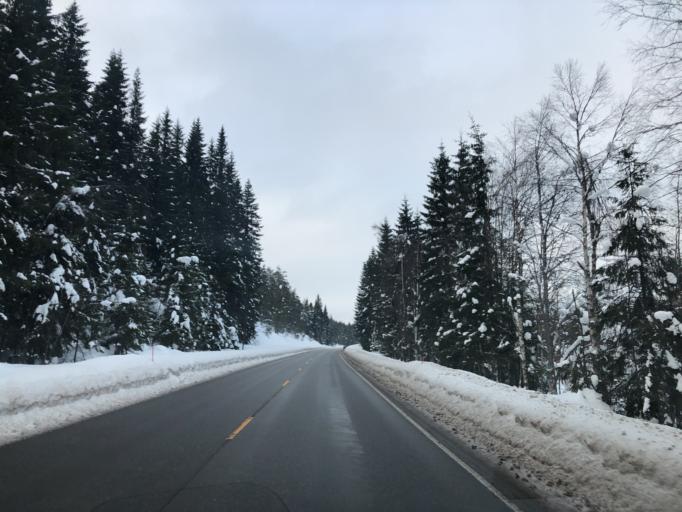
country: NO
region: Hedmark
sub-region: Trysil
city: Innbygda
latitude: 61.2768
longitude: 12.2881
